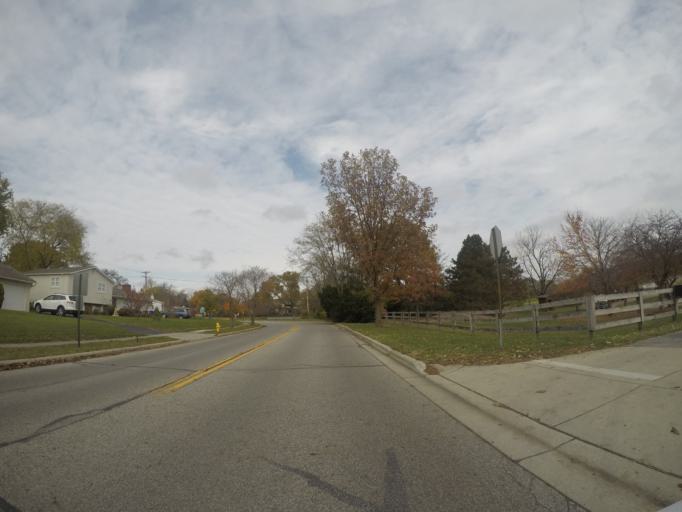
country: US
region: Ohio
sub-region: Franklin County
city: Upper Arlington
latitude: 40.0128
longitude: -83.0468
